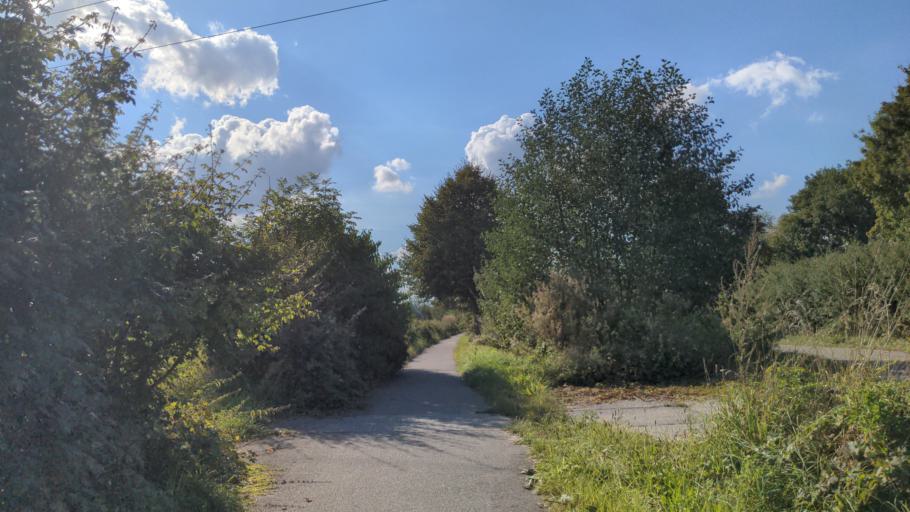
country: DE
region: Schleswig-Holstein
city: Badendorf
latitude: 53.8730
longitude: 10.6026
